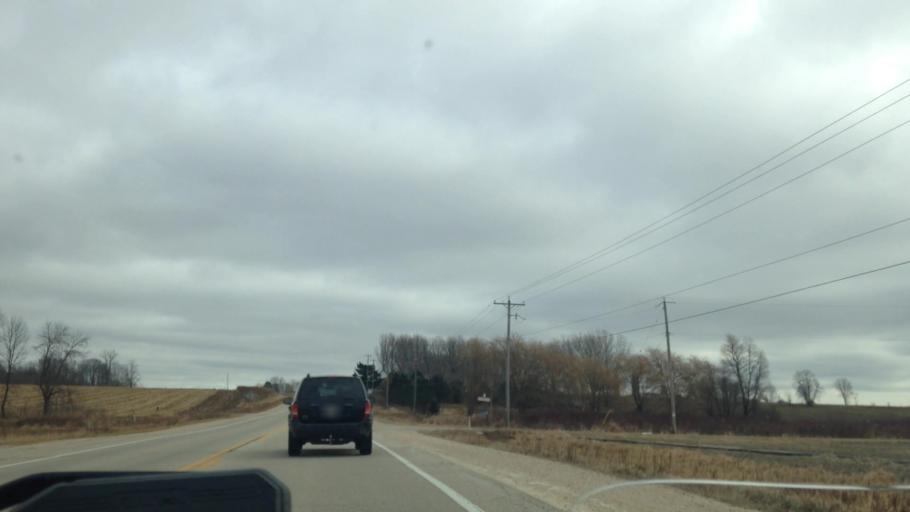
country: US
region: Wisconsin
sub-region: Dodge County
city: Theresa
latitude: 43.4214
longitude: -88.4068
